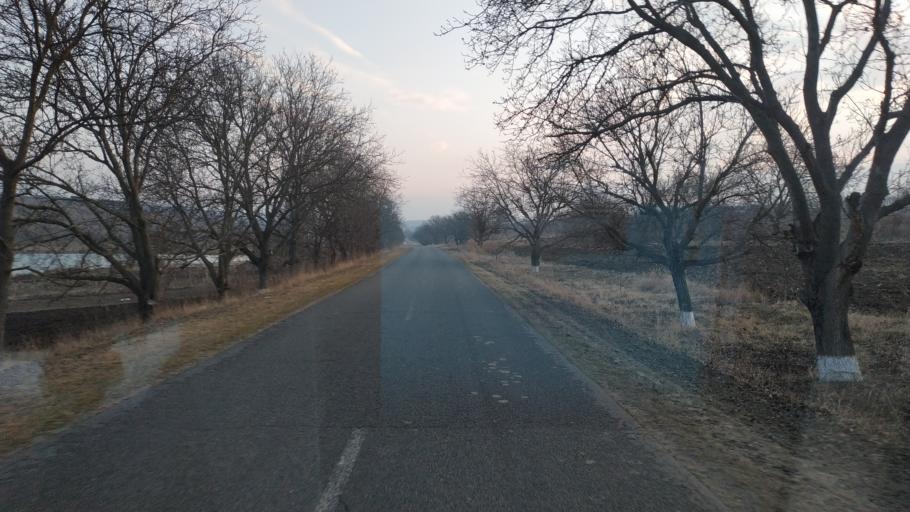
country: MD
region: Hincesti
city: Dancu
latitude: 46.6967
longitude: 28.3365
